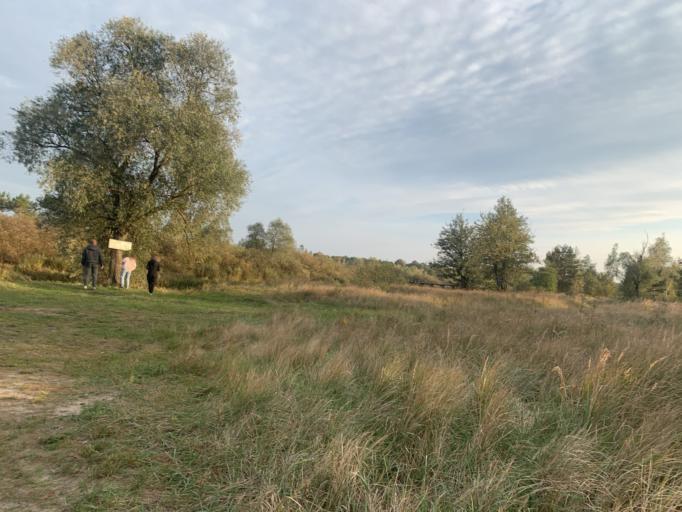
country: BY
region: Brest
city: Mikashevichy
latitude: 52.3321
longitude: 27.4979
